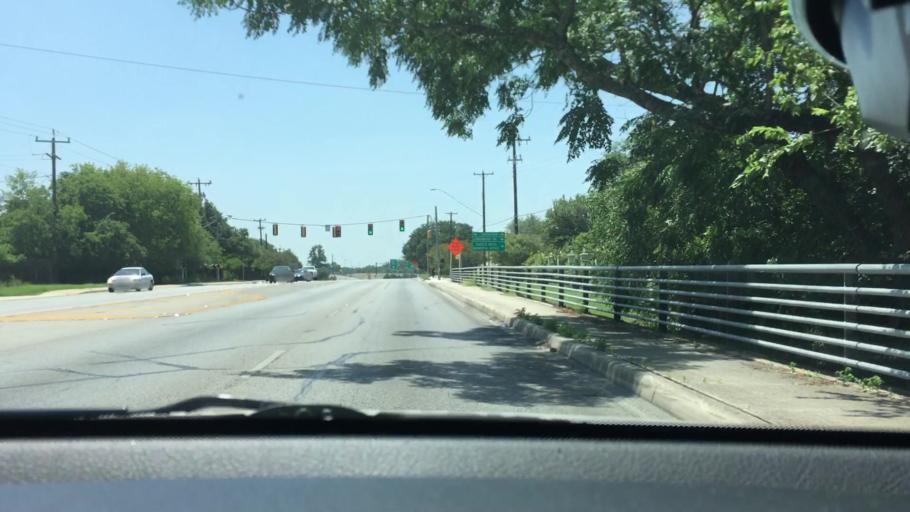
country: US
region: Texas
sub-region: Bexar County
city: Castle Hills
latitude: 29.5252
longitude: -98.5169
